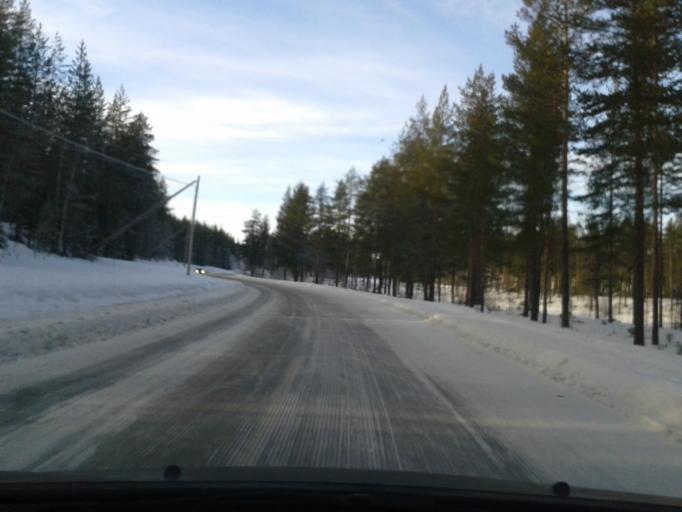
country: SE
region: Vaesternorrland
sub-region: OErnskoeldsviks Kommun
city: Bredbyn
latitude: 63.6566
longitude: 17.8715
